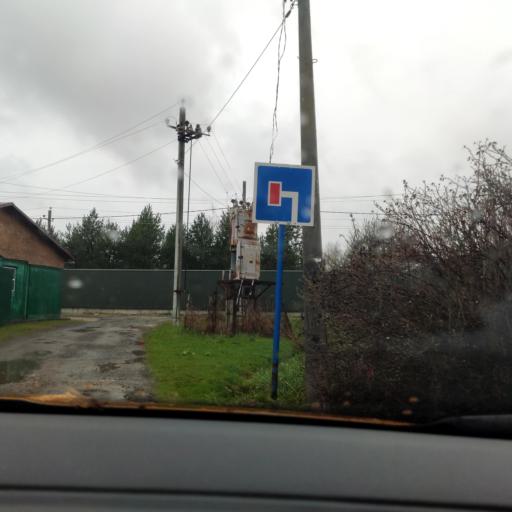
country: RU
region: Moskovskaya
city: Zvenigorod
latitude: 55.7511
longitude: 36.8675
